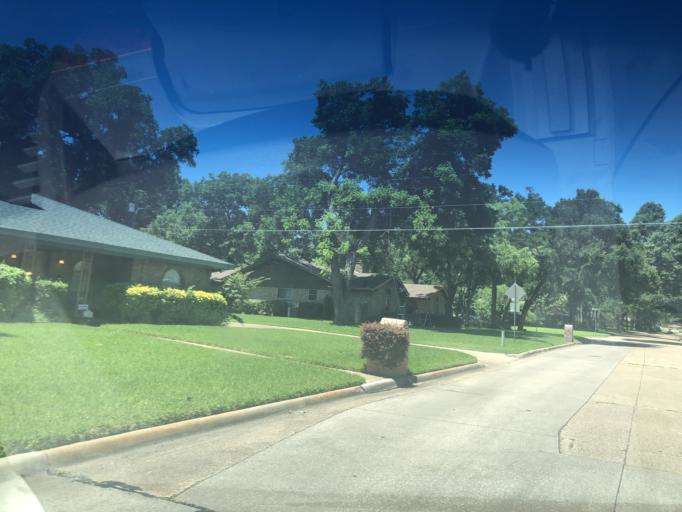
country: US
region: Texas
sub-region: Dallas County
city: Grand Prairie
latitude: 32.7731
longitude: -97.0358
